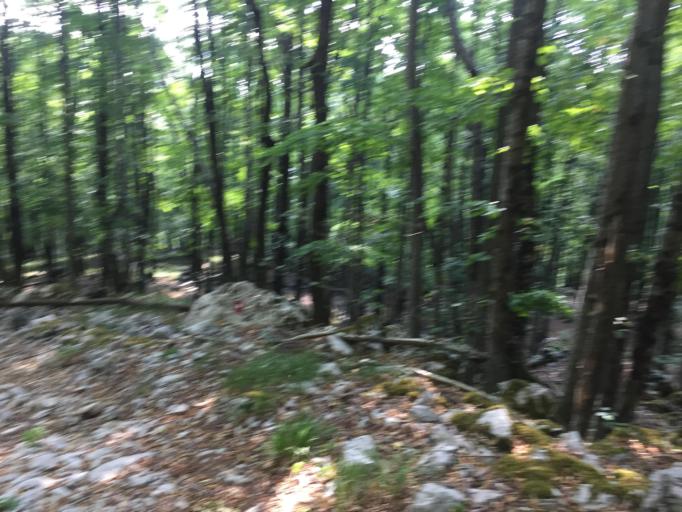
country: HR
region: Primorsko-Goranska
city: Klana
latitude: 45.4617
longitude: 14.4350
